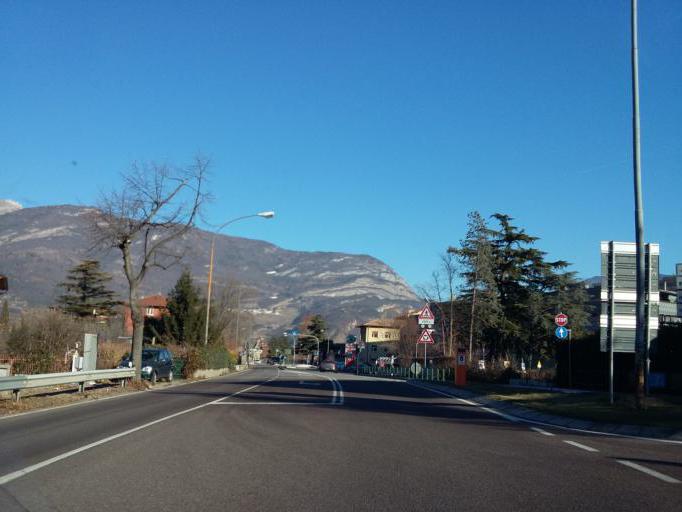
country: IT
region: Trentino-Alto Adige
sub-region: Provincia di Trento
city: Villa Lagarina
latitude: 45.9071
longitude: 11.0399
